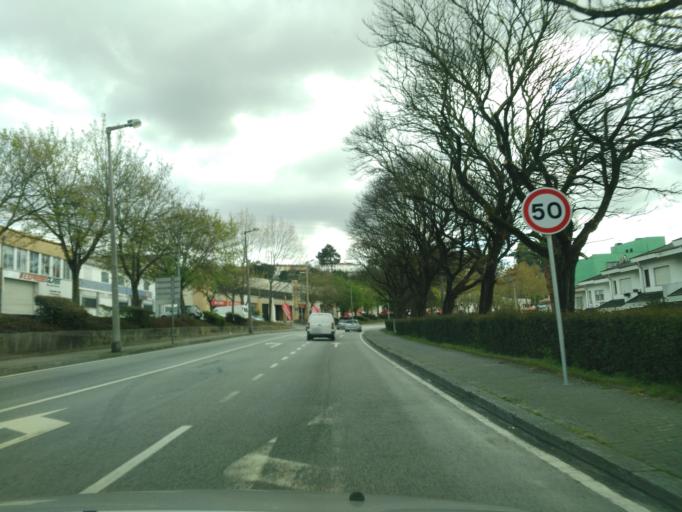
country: PT
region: Braga
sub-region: Guimaraes
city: Urgeses
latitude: 41.4306
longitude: -8.3022
